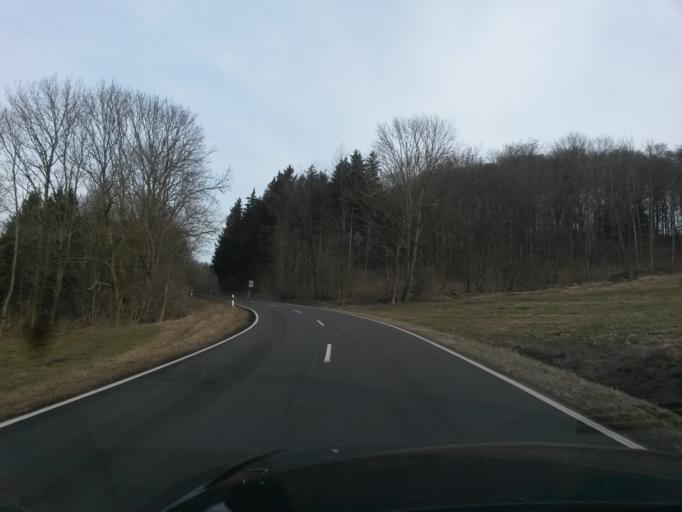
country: DE
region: Hesse
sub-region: Regierungsbezirk Kassel
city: Hilders
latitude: 50.5805
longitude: 10.0148
